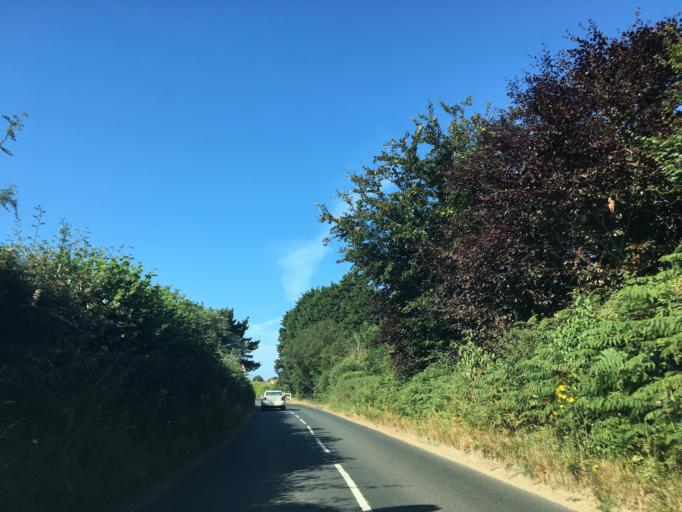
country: GB
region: England
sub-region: Isle of Wight
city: Chale
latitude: 50.6175
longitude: -1.3141
